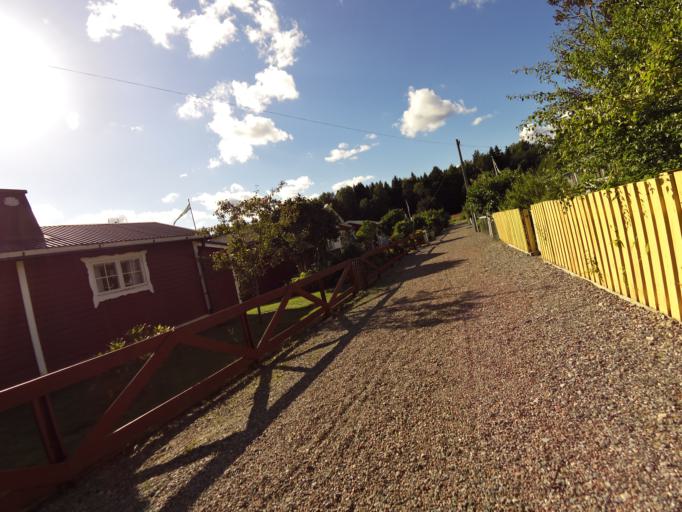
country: SE
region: Gaevleborg
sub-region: Gavle Kommun
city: Gavle
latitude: 60.7082
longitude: 17.1589
